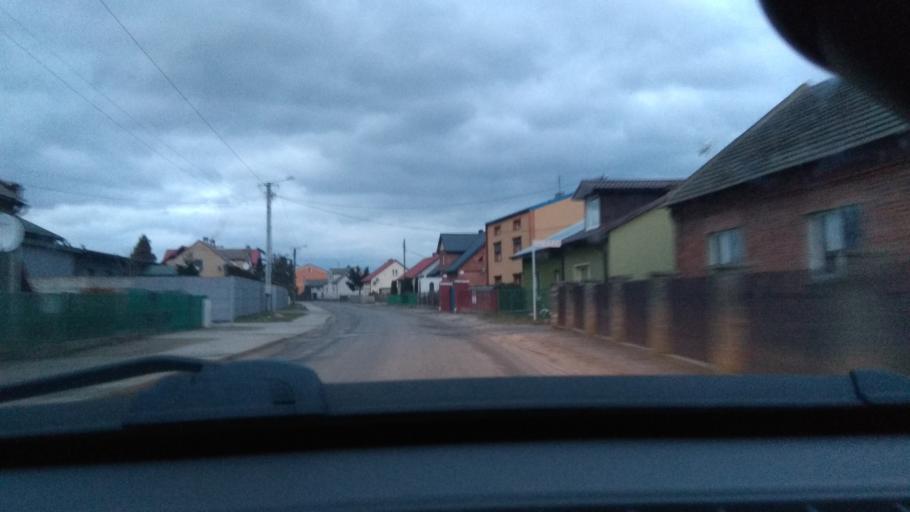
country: PL
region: Lodz Voivodeship
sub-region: Powiat wieruszowski
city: Wieruszow
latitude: 51.3041
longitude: 18.0808
